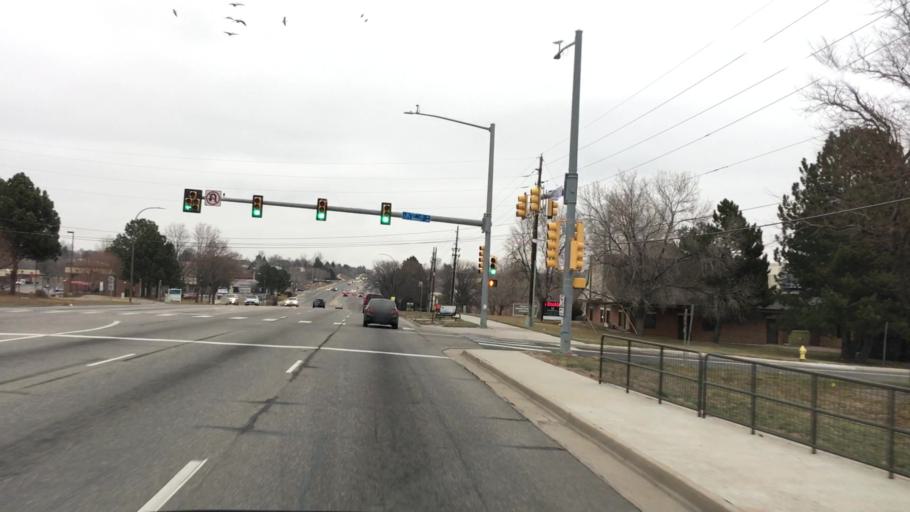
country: US
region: Colorado
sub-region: Jefferson County
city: Arvada
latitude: 39.8375
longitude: -105.0817
